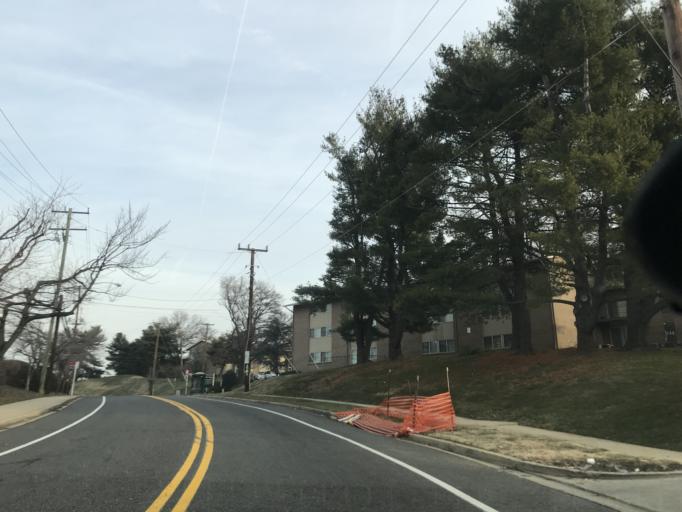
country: US
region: Maryland
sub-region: Prince George's County
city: Lanham
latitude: 38.9553
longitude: -76.8683
